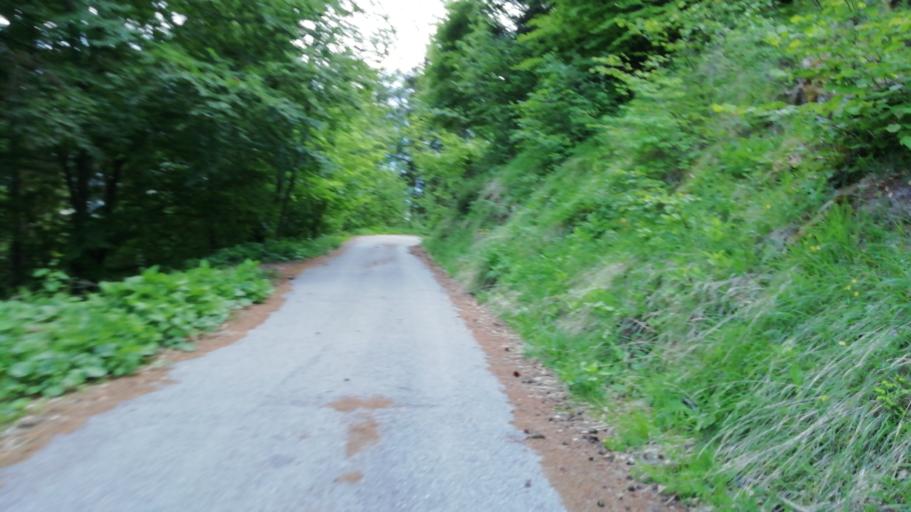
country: IT
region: Veneto
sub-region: Provincia di Belluno
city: Valle di Cadore
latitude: 46.4234
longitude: 12.3240
